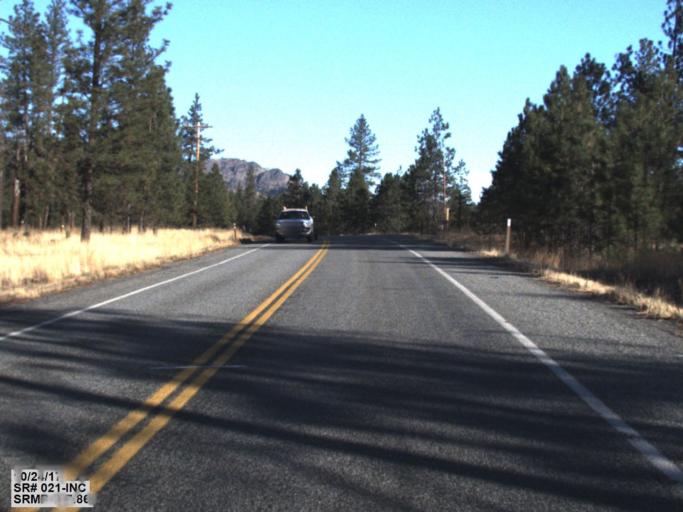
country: US
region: Washington
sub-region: Okanogan County
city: Coulee Dam
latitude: 48.0928
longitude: -118.6918
